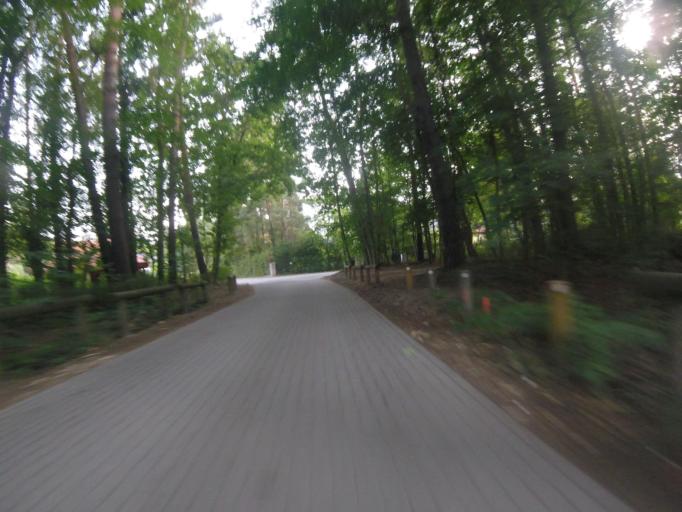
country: DE
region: Brandenburg
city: Zeuthen
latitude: 52.3500
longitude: 13.6106
